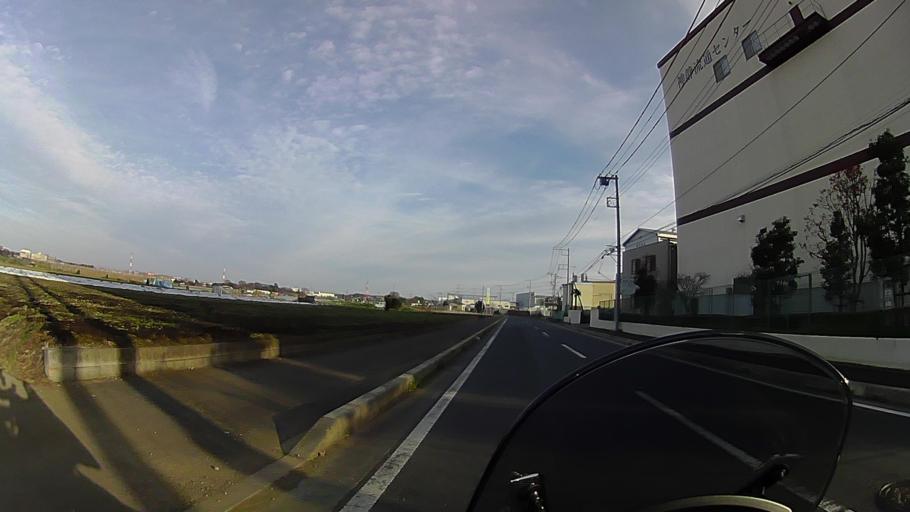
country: JP
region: Kanagawa
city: Minami-rinkan
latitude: 35.4280
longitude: 139.4224
